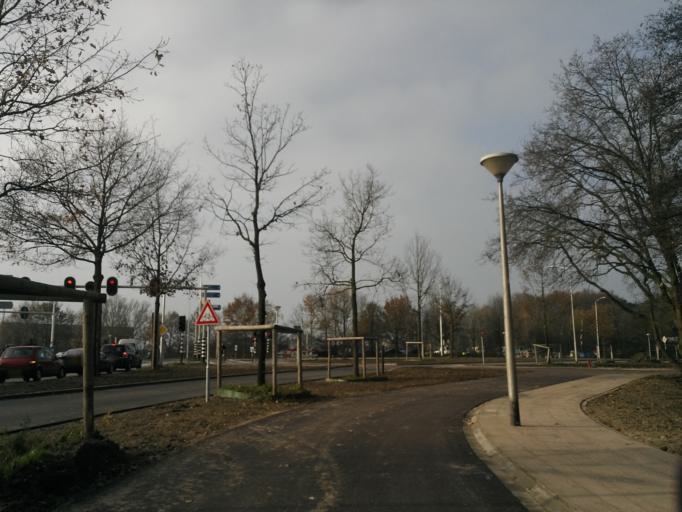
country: NL
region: Utrecht
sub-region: Gemeente Amersfoort
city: Amersfoort
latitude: 52.1665
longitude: 5.3764
